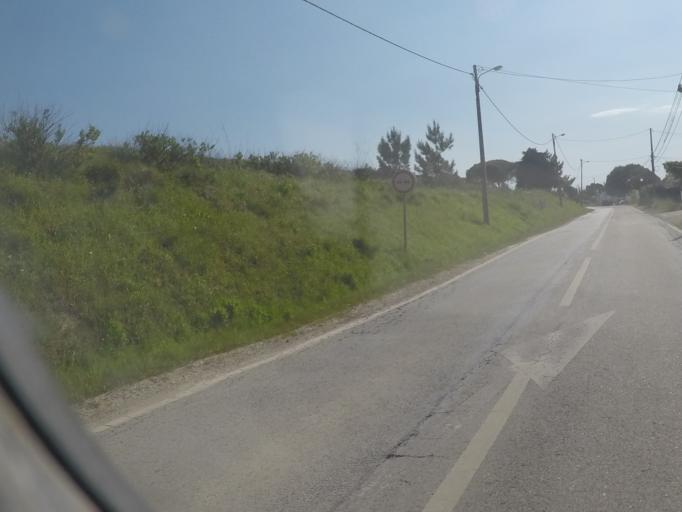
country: PT
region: Setubal
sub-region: Sesimbra
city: Sesimbra
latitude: 38.4437
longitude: -9.1680
